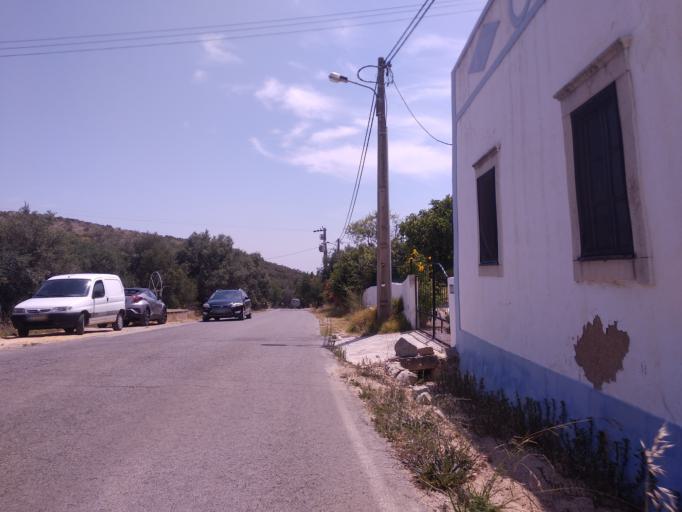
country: PT
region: Faro
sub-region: Faro
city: Santa Barbara de Nexe
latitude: 37.1117
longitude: -7.9464
